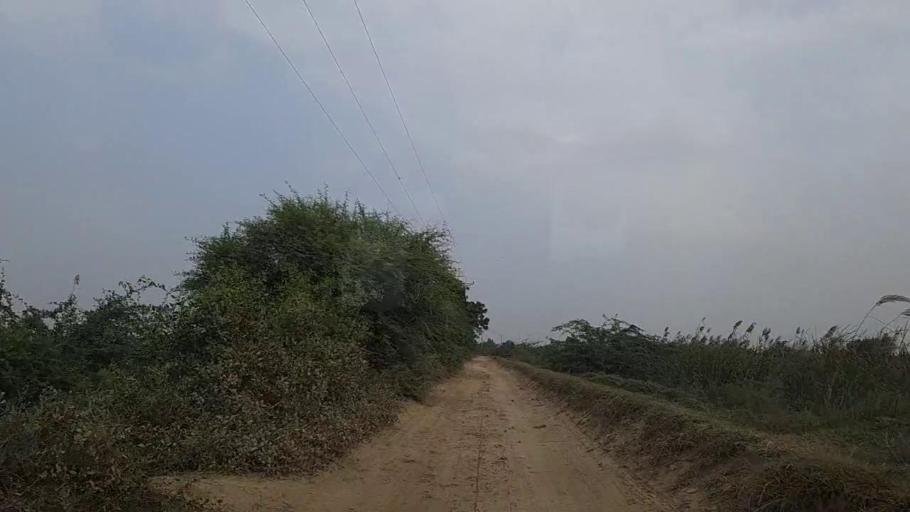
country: PK
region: Sindh
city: Mirpur Sakro
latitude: 24.6097
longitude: 67.7097
